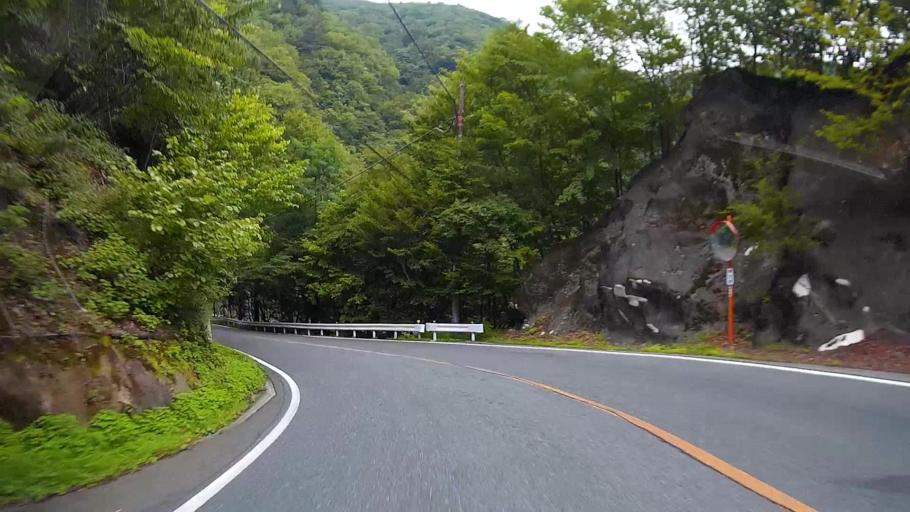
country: JP
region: Yamanashi
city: Enzan
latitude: 35.9227
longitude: 138.8285
